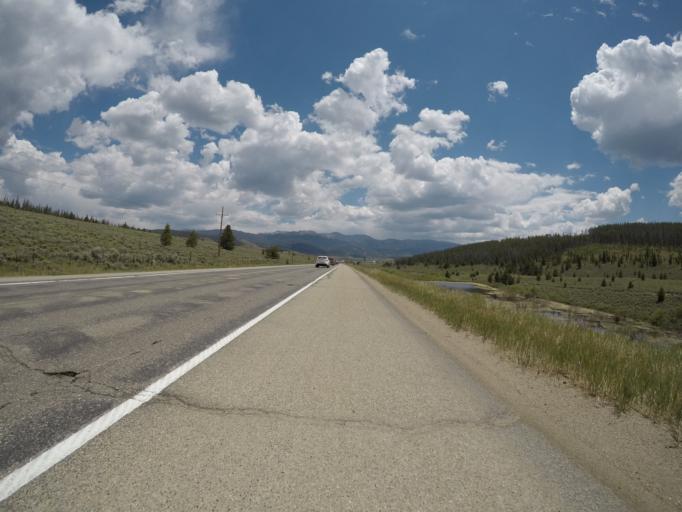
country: US
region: Colorado
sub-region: Grand County
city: Fraser
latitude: 39.9949
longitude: -105.8657
